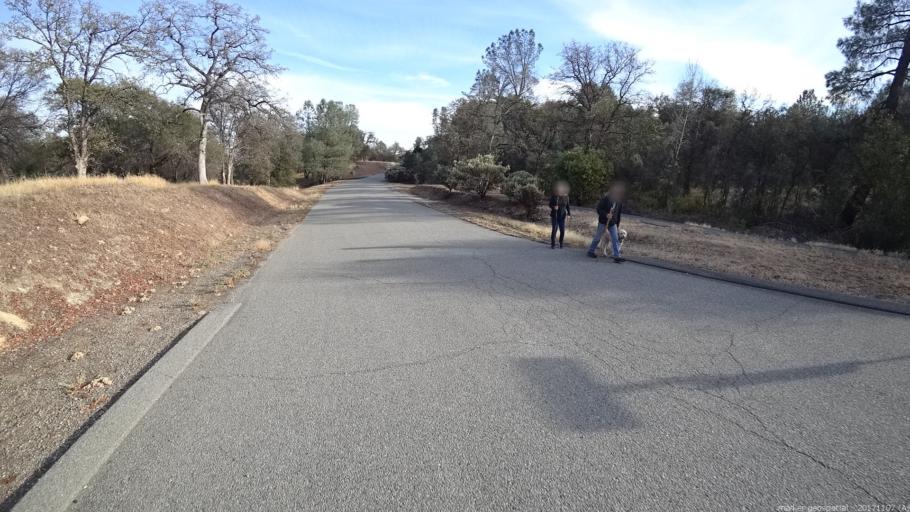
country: US
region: California
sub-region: Shasta County
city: Shasta
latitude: 40.5099
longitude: -122.4704
